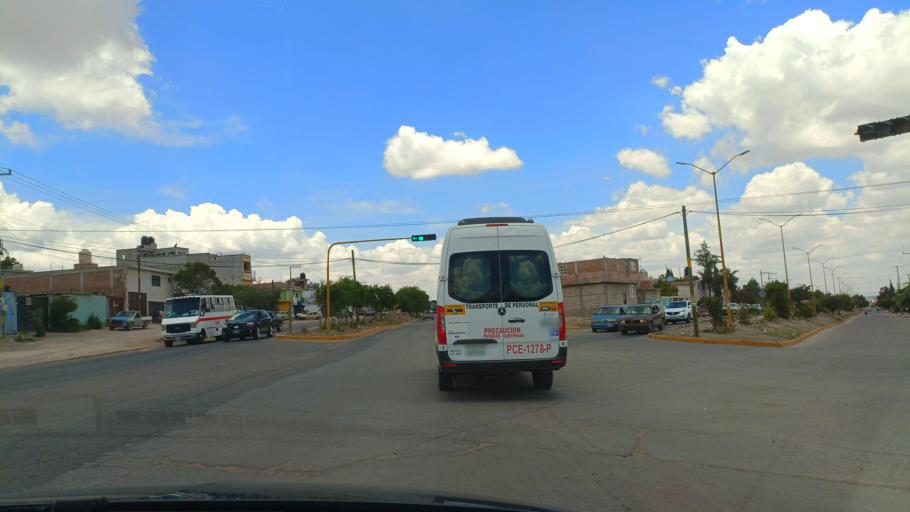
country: MX
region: Guerrero
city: San Luis de la Paz
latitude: 21.2892
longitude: -100.5055
